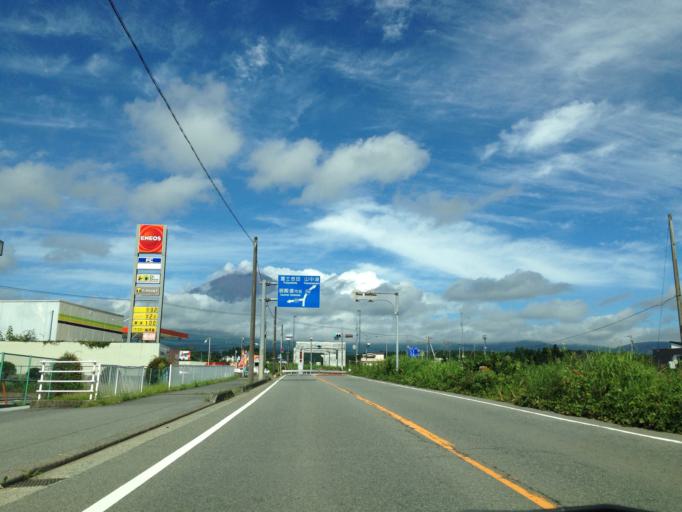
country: JP
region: Shizuoka
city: Gotemba
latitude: 35.3187
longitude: 138.9159
